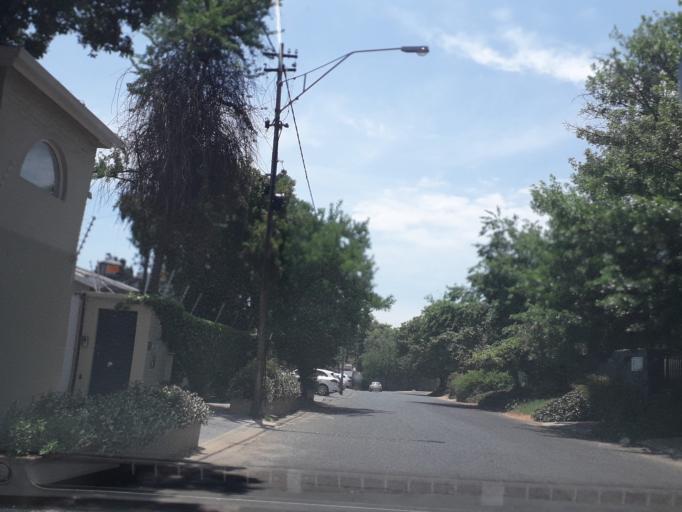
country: ZA
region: Gauteng
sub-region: City of Johannesburg Metropolitan Municipality
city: Johannesburg
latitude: -26.1352
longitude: 28.0290
